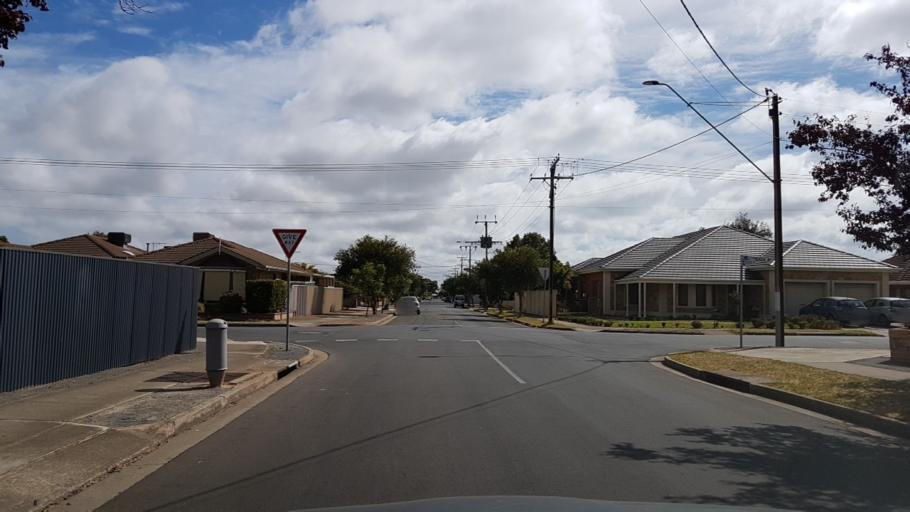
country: AU
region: South Australia
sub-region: Marion
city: Plympton Park
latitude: -34.9896
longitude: 138.5504
